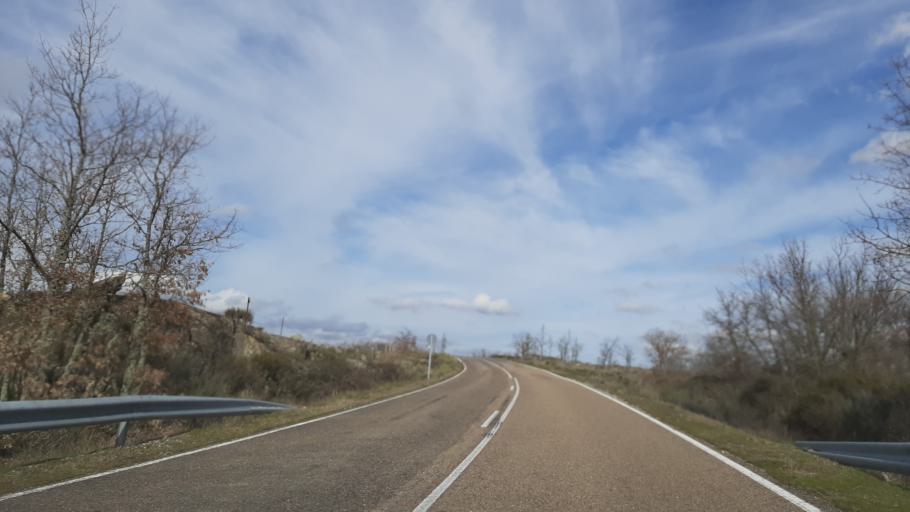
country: ES
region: Castille and Leon
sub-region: Provincia de Salamanca
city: Villarino de los Aires
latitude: 41.2483
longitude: -6.4949
